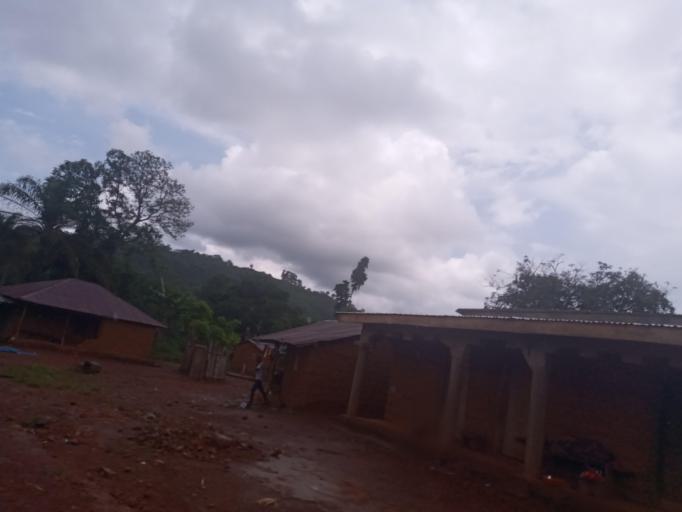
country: SL
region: Northern Province
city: Bumbuna
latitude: 8.9202
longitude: -11.7412
